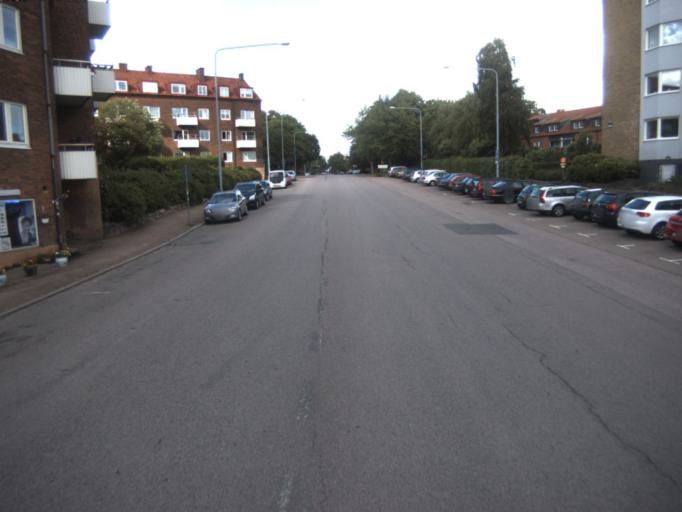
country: SE
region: Skane
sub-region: Helsingborg
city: Helsingborg
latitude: 56.0448
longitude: 12.7093
